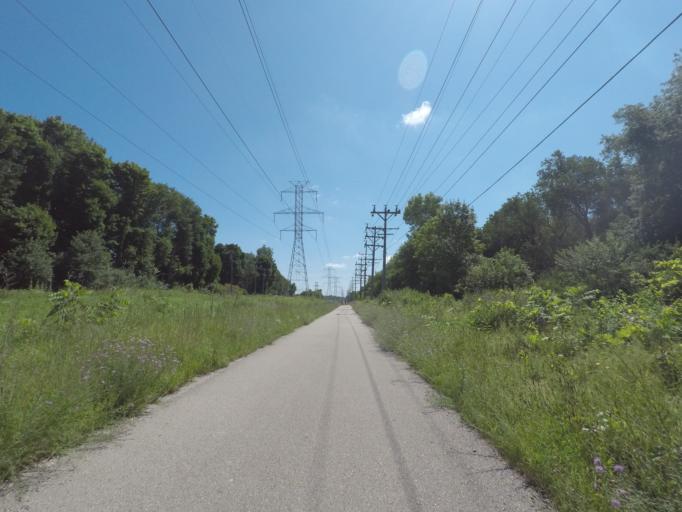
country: US
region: Wisconsin
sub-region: Waukesha County
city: Elm Grove
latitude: 43.0101
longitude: -88.0602
